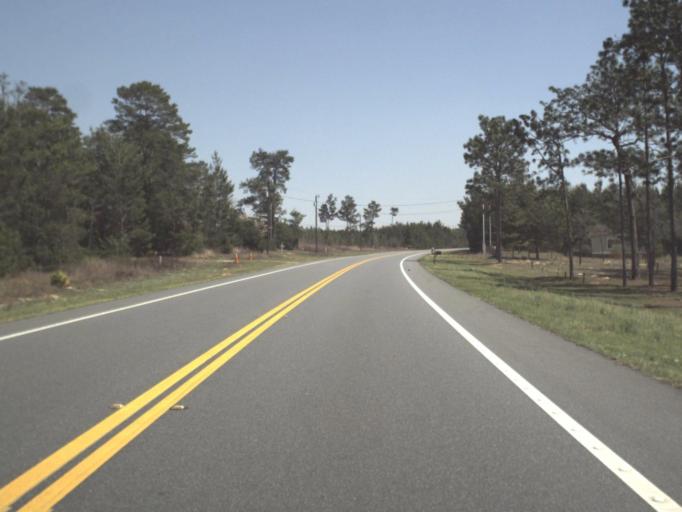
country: US
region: Florida
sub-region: Bay County
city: Youngstown
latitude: 30.4371
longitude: -85.3422
